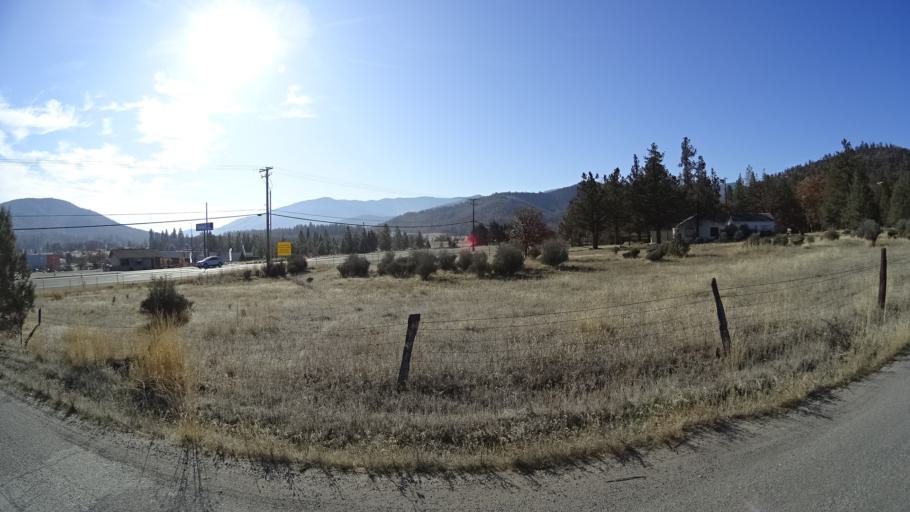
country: US
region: California
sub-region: Siskiyou County
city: Yreka
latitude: 41.6996
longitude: -122.6479
